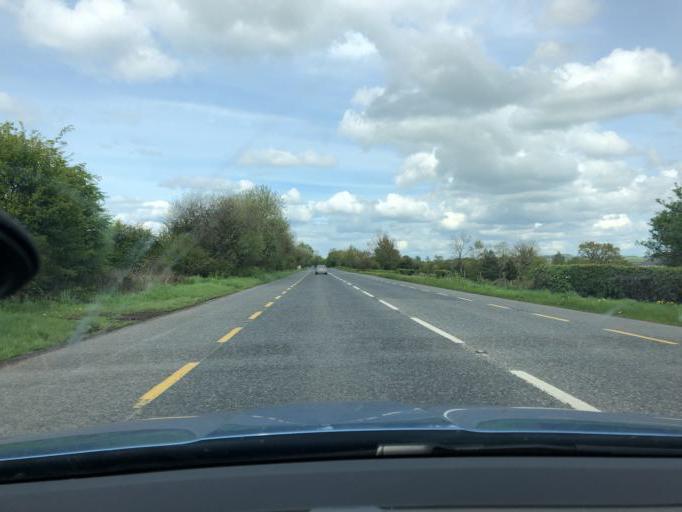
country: IE
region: Leinster
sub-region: Laois
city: Portlaoise
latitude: 52.9790
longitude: -7.3224
